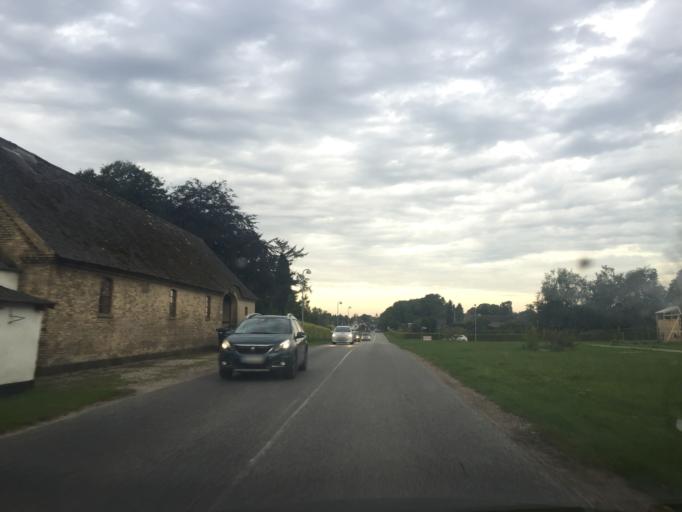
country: DK
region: Zealand
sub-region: Roskilde Kommune
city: Gundsomagle
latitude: 55.7337
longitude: 12.1623
